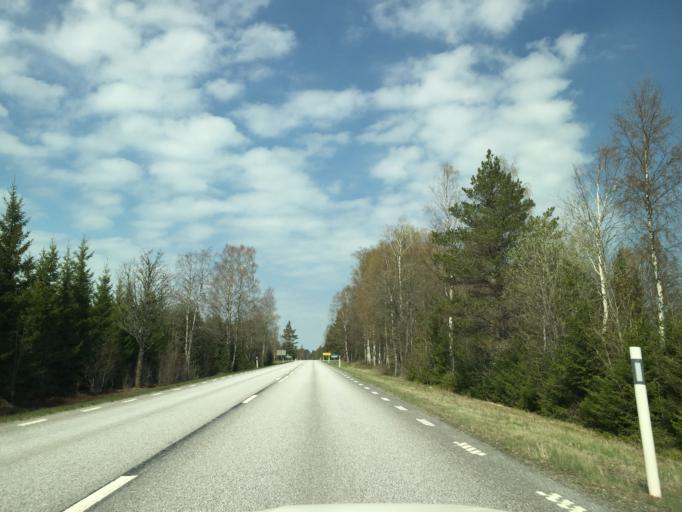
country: SE
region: Vaestra Goetaland
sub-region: Bengtsfors Kommun
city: Dals Langed
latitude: 58.8100
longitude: 12.1472
